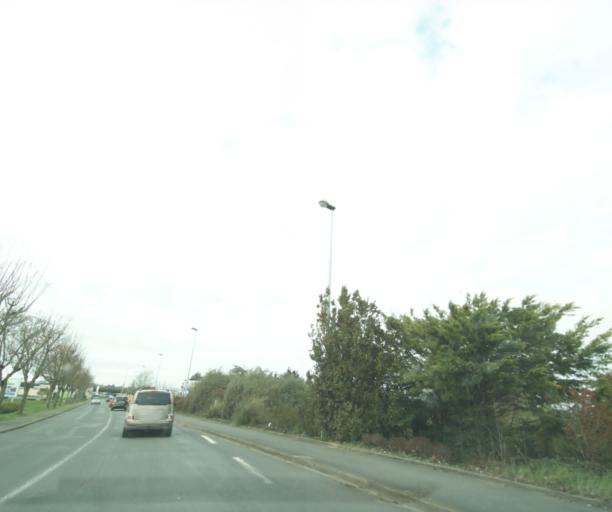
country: FR
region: Poitou-Charentes
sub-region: Departement de la Charente-Maritime
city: La Rochelle
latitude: 46.1721
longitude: -1.1647
